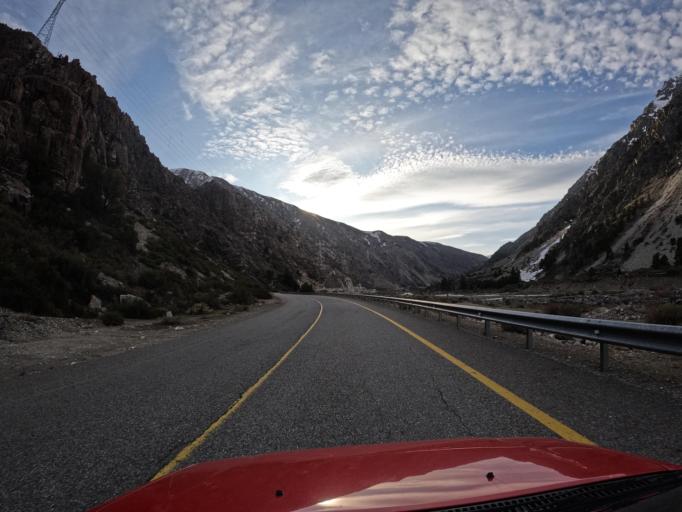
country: CL
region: Maule
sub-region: Provincia de Linares
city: Colbun
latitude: -35.8803
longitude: -70.6667
